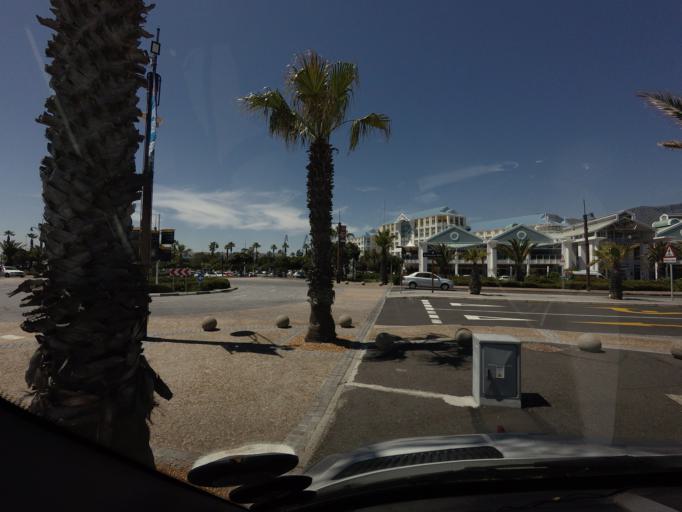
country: ZA
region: Western Cape
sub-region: City of Cape Town
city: Cape Town
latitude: -33.9016
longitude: 18.4211
